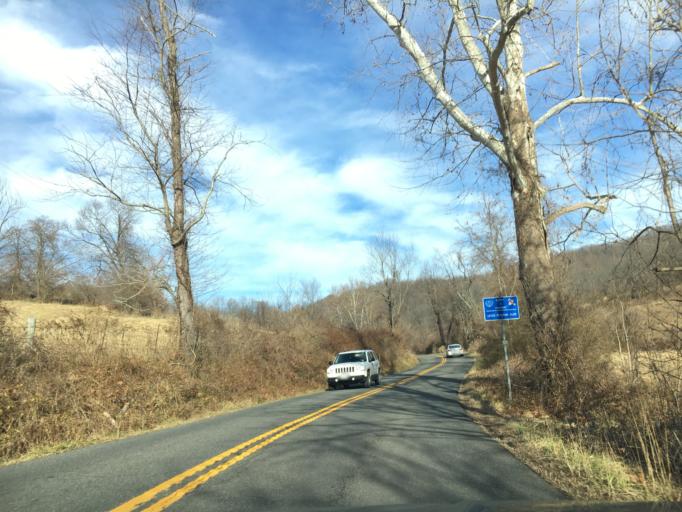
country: US
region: Virginia
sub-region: Warren County
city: Apple Mountain Lake
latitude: 38.8812
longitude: -78.0035
